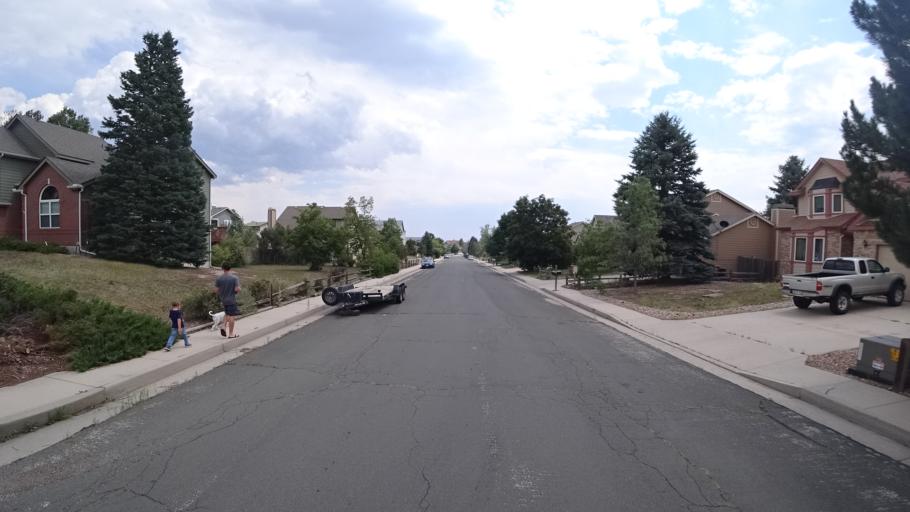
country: US
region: Colorado
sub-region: El Paso County
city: Black Forest
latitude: 38.9576
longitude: -104.7439
